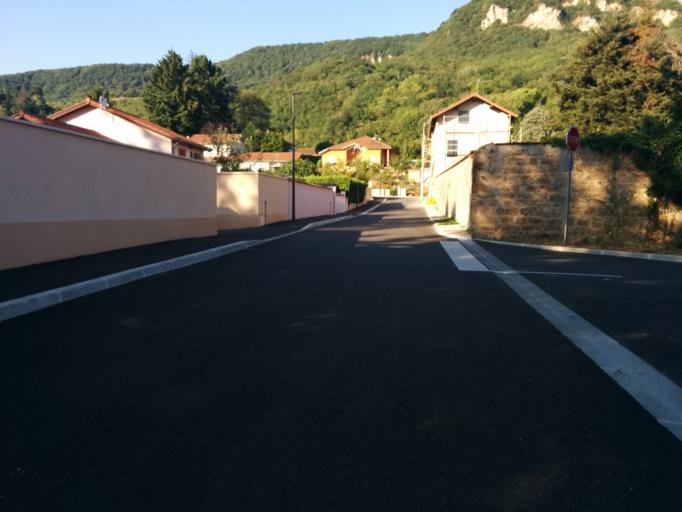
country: FR
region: Rhone-Alpes
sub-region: Departement de l'Ain
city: Lagnieu
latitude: 45.8963
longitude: 5.3543
